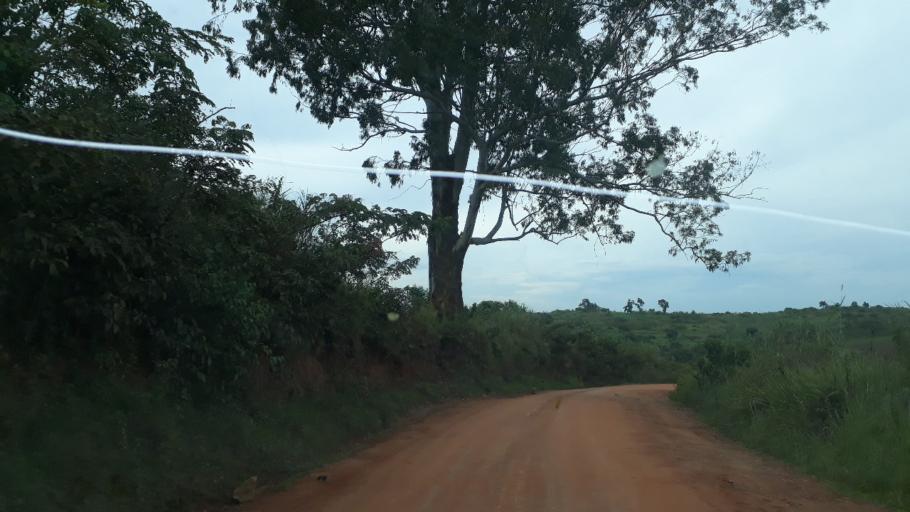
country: UG
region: Northern Region
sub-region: Zombo District
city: Paidha
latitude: 2.0652
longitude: 30.6242
